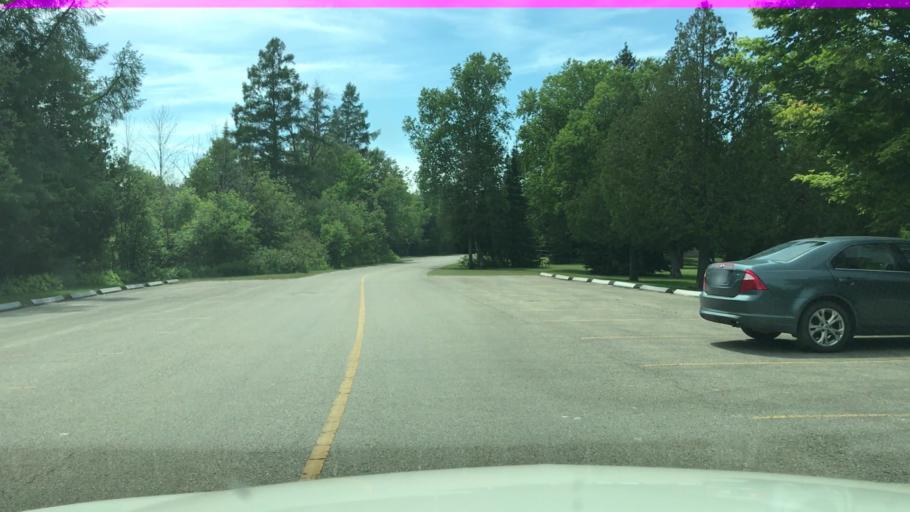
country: US
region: Michigan
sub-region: Schoolcraft County
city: Manistique
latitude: 45.9440
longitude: -86.3347
